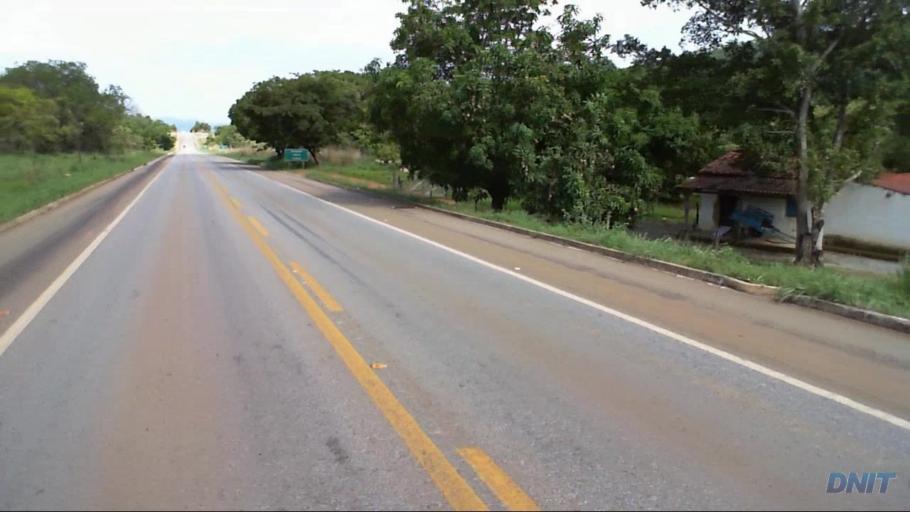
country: BR
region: Goias
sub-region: Barro Alto
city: Barro Alto
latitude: -15.1425
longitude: -48.8207
